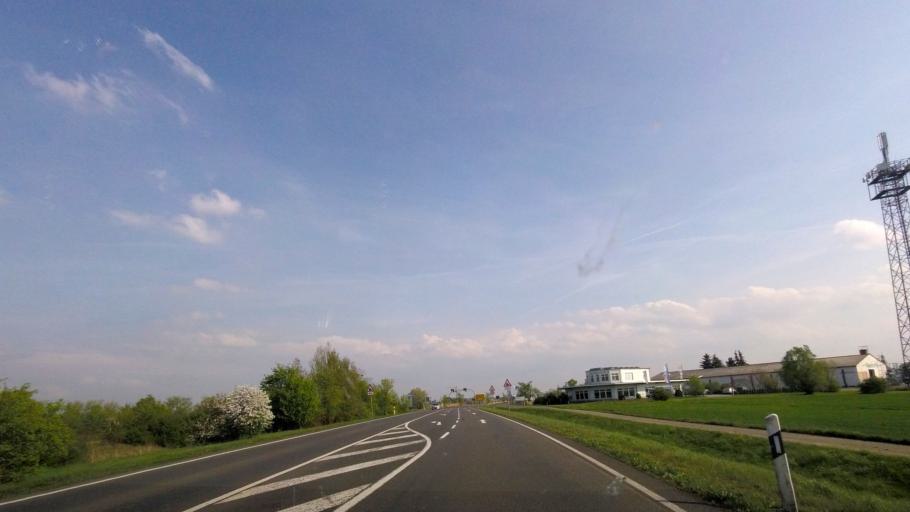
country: DE
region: Saxony-Anhalt
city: Wittenburg
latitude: 51.8285
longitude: 12.6365
